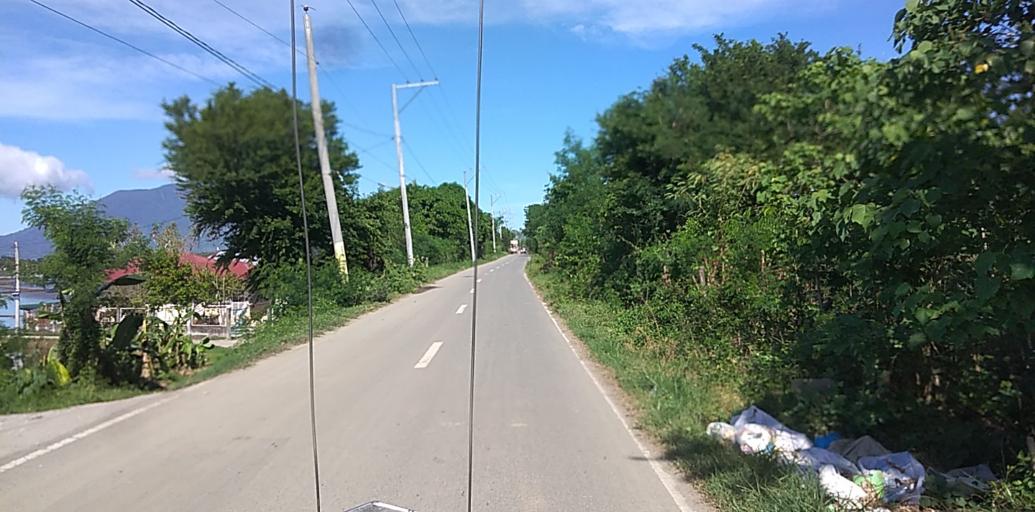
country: PH
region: Central Luzon
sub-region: Province of Pampanga
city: Candaba
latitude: 15.1165
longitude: 120.8146
